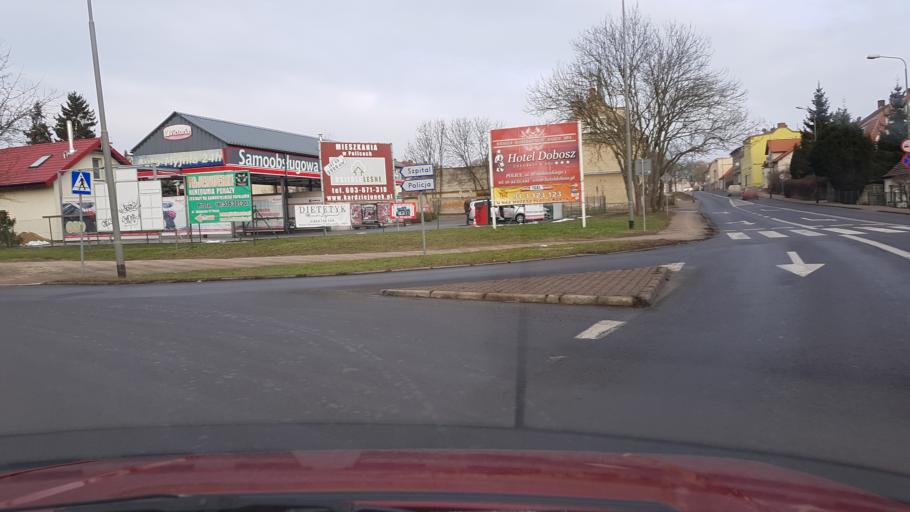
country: PL
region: West Pomeranian Voivodeship
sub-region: Powiat policki
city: Police
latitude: 53.5443
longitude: 14.5754
